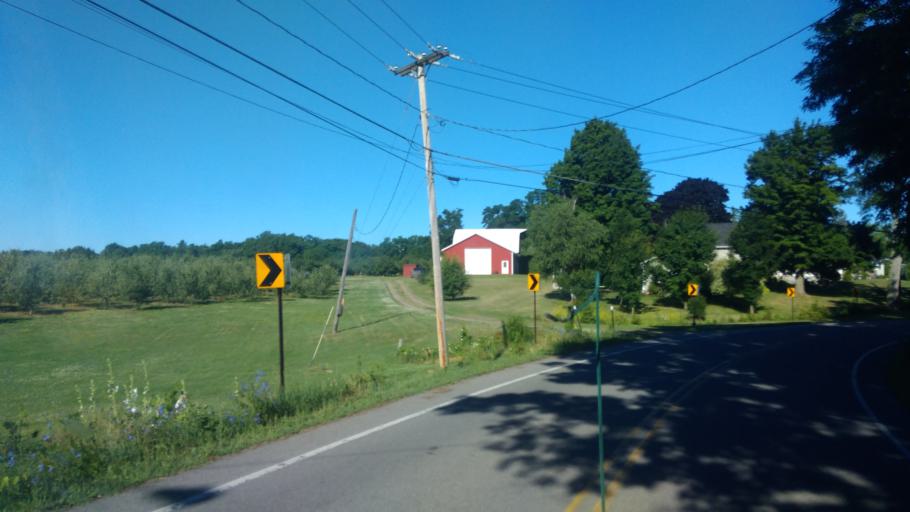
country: US
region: New York
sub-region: Wayne County
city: Williamson
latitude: 43.2802
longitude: -77.1735
